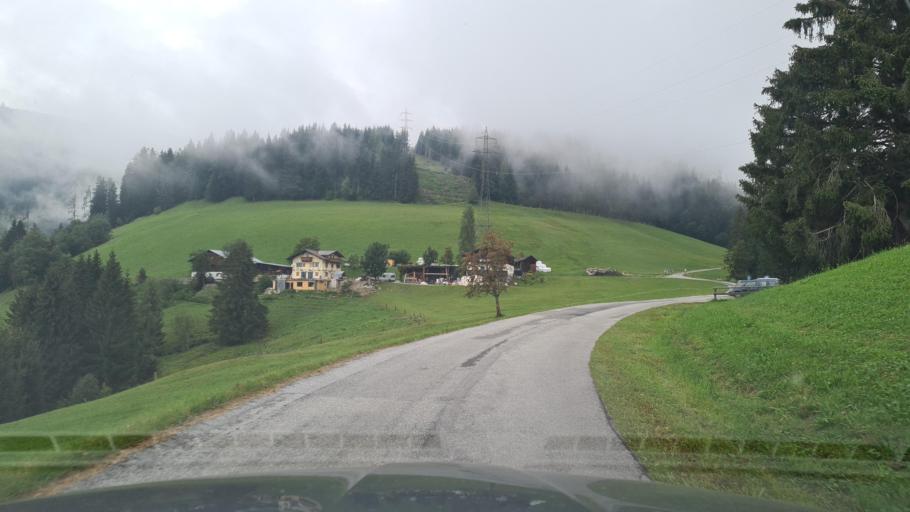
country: AT
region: Salzburg
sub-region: Politischer Bezirk Sankt Johann im Pongau
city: Sankt Johann im Pongau
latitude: 47.3590
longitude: 13.1725
